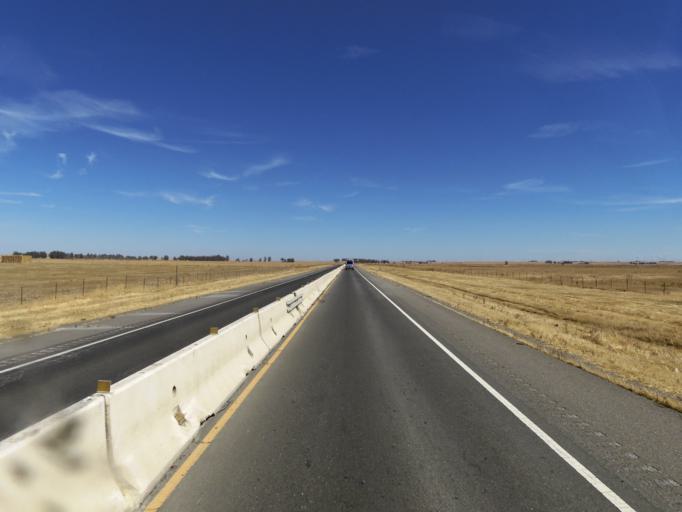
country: US
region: California
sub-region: Solano County
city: Suisun
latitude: 38.2284
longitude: -121.9360
